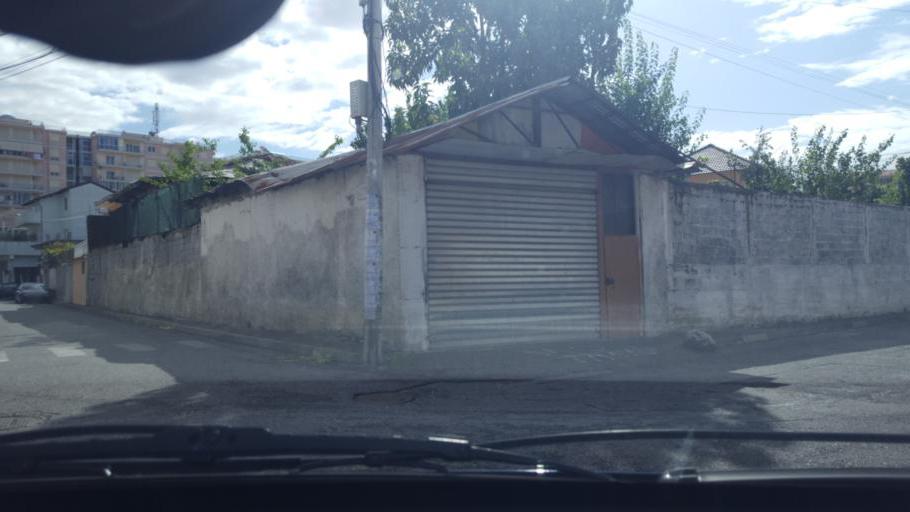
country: AL
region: Shkoder
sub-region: Rrethi i Shkodres
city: Shkoder
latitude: 42.0737
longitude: 19.5077
